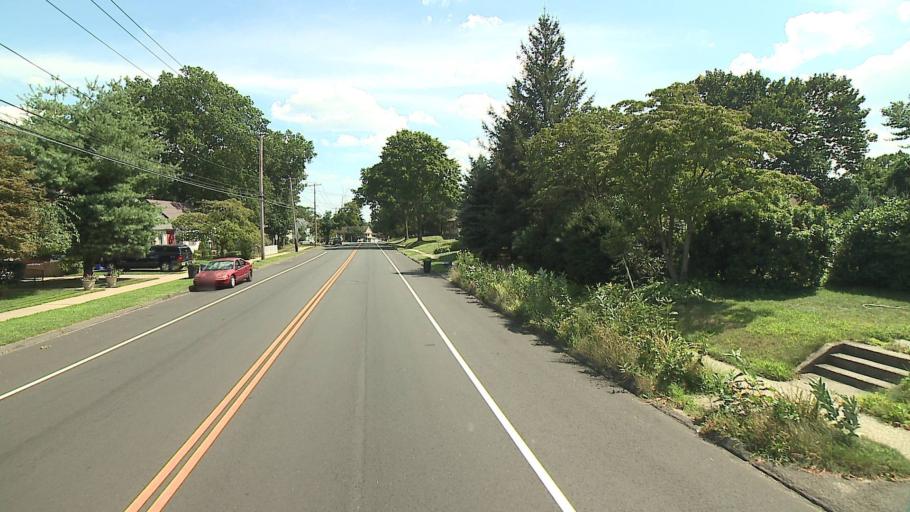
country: US
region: Connecticut
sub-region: Fairfield County
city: Stratford
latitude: 41.2008
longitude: -73.1377
